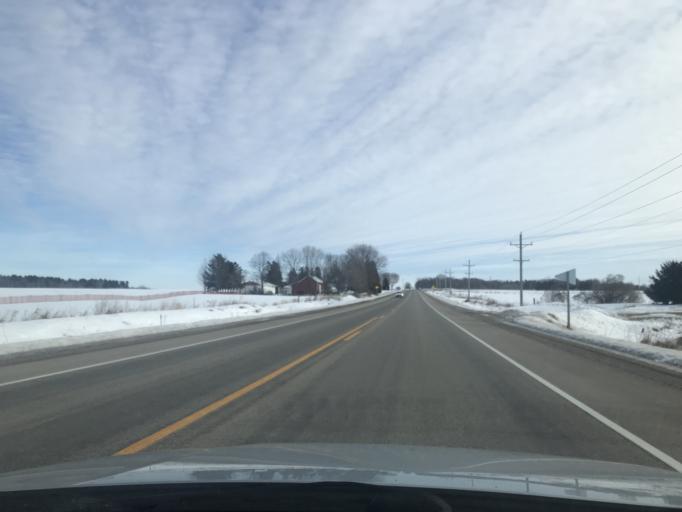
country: US
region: Wisconsin
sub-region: Oconto County
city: Oconto Falls
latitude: 44.8946
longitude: -88.1805
